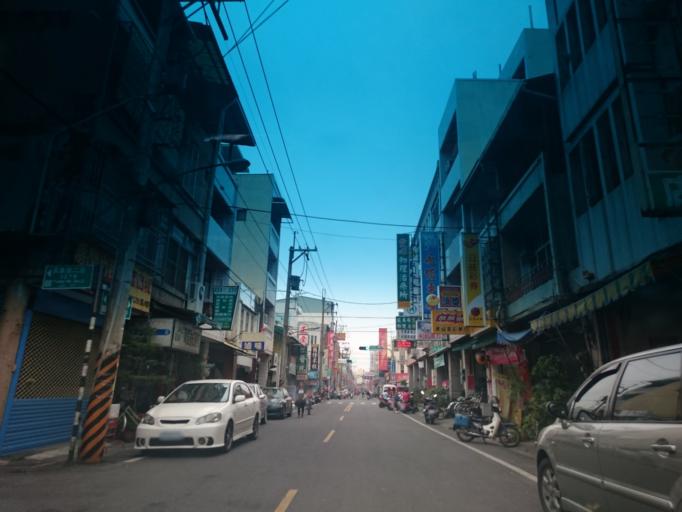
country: TW
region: Taiwan
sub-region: Nantou
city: Nantou
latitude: 23.8573
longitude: 120.5860
